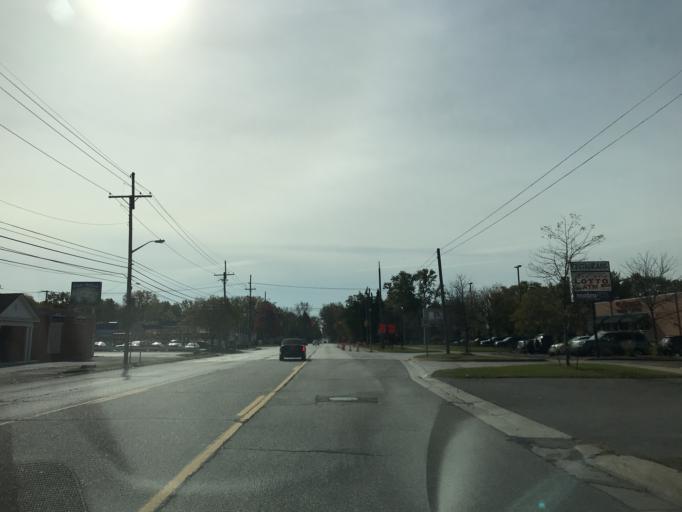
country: US
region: Michigan
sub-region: Oakland County
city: Southfield
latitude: 42.4593
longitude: -83.2602
